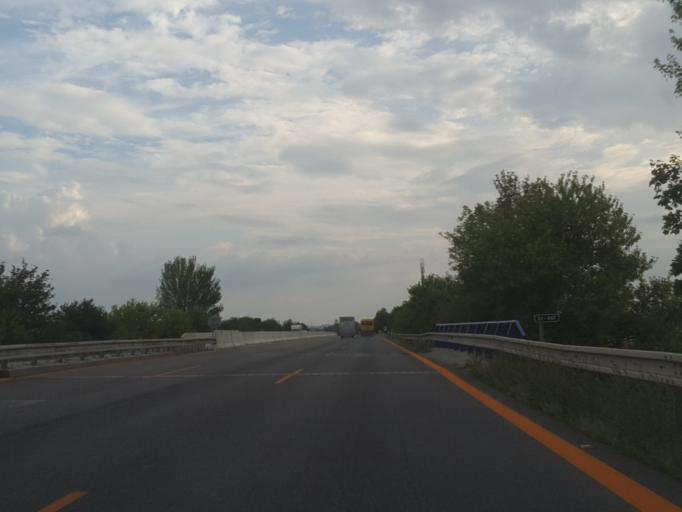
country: SK
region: Bratislavsky
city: Senec
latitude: 48.2773
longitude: 17.4683
